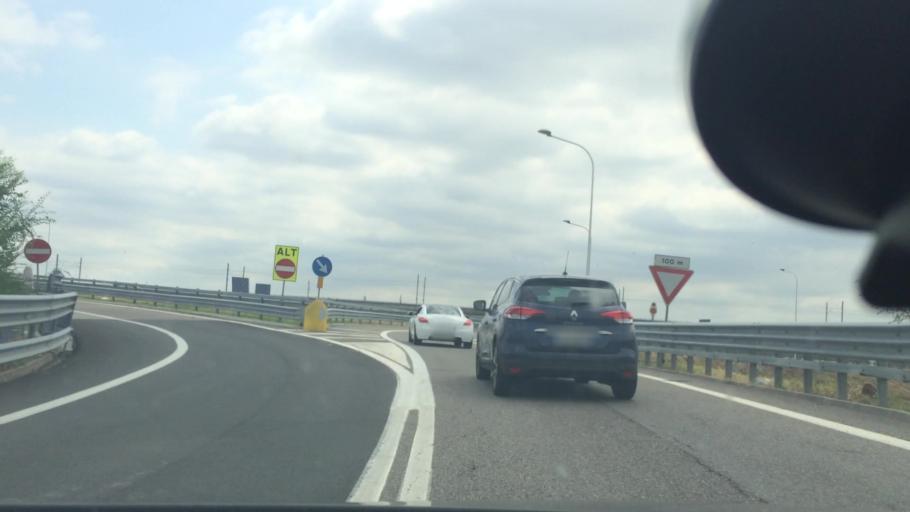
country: IT
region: Lombardy
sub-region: Citta metropolitana di Milano
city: Rho
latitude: 45.5228
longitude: 9.0586
